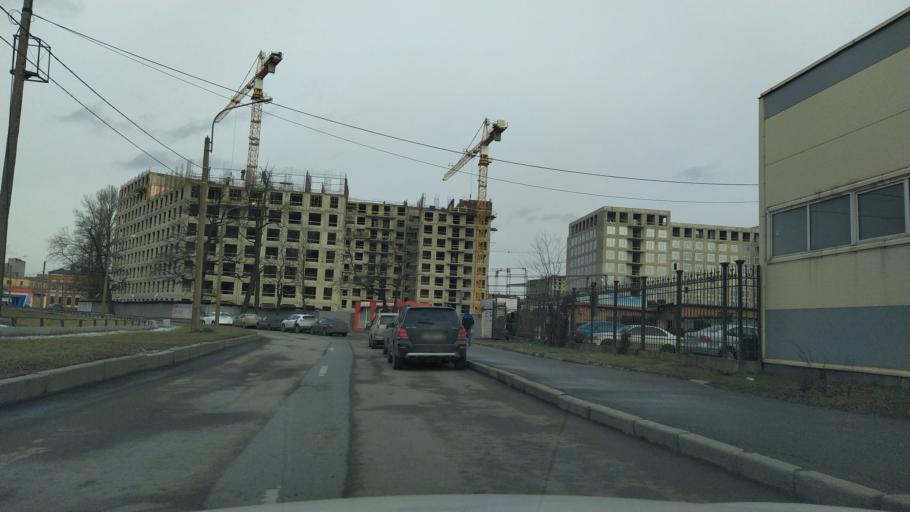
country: RU
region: Leningrad
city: Chernaya Rechka
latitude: 59.9814
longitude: 30.3187
